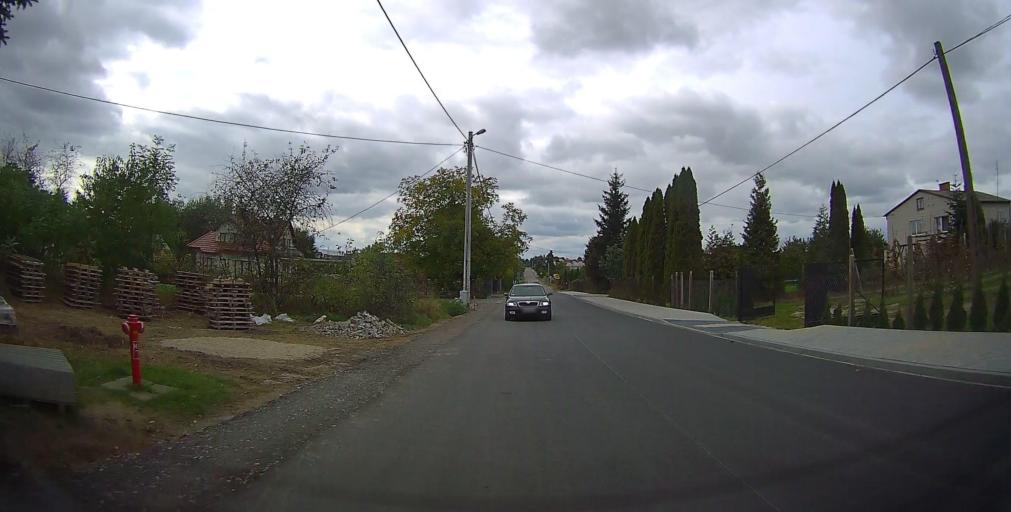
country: PL
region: Masovian Voivodeship
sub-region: Powiat grojecki
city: Belsk Duzy
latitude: 51.8142
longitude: 20.8307
